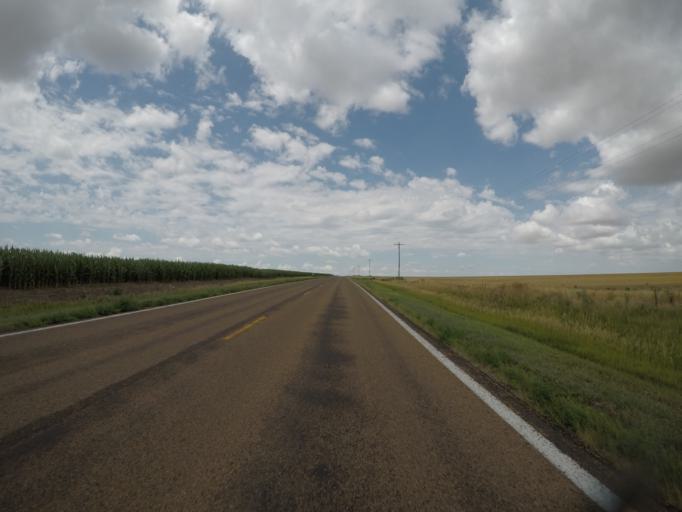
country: US
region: Kansas
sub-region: Rawlins County
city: Atwood
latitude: 39.9359
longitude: -101.0561
